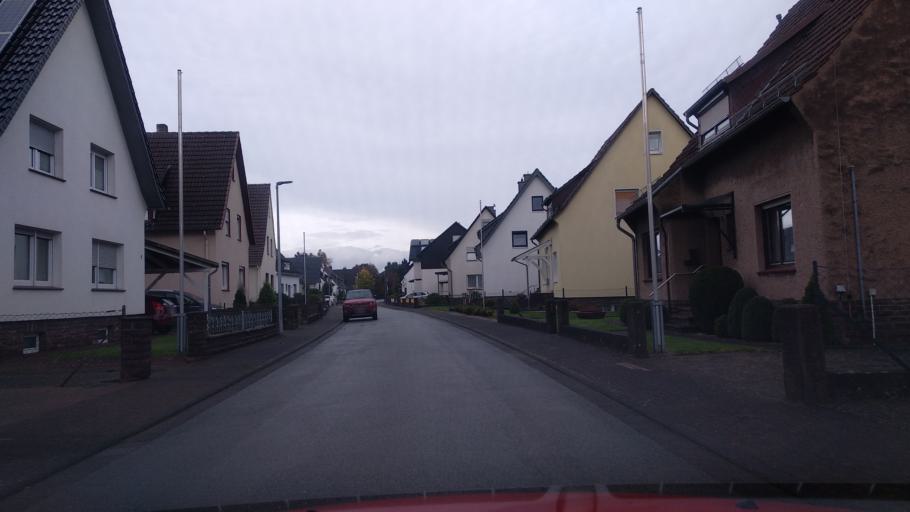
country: DE
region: North Rhine-Westphalia
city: Beverungen
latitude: 51.6700
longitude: 9.3784
